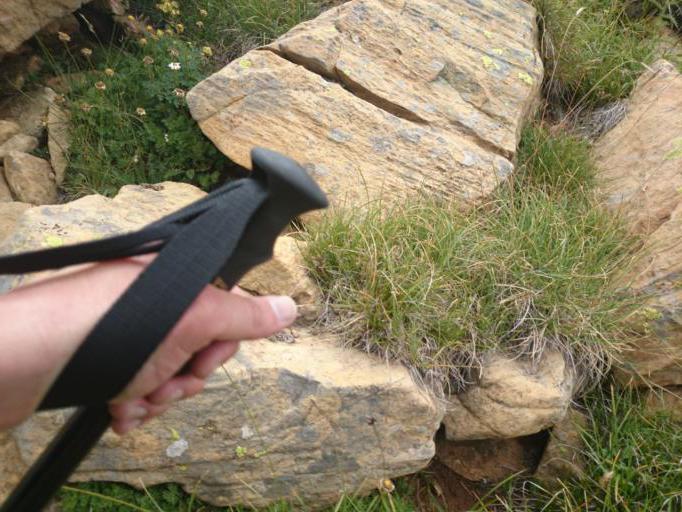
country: AL
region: Diber
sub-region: Rrethi i Dibres
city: Fushe-Lure
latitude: 41.7850
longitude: 20.1826
